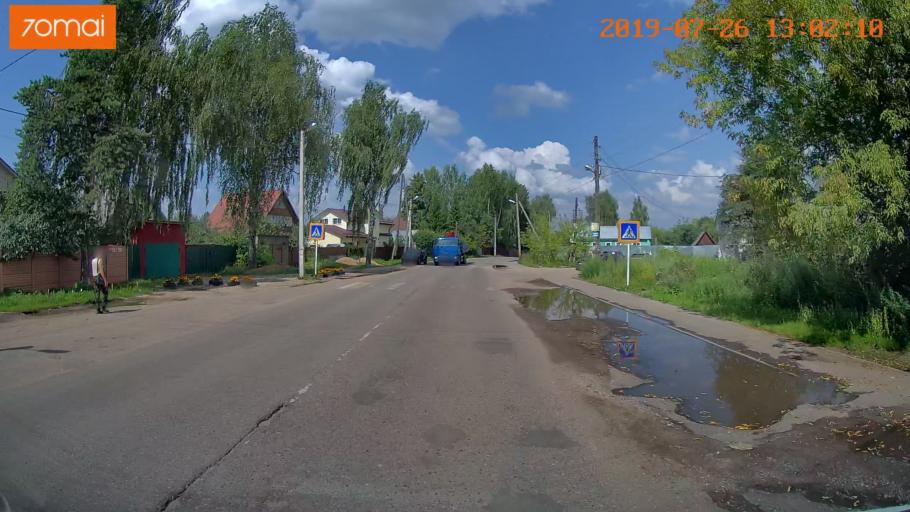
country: RU
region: Ivanovo
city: Bogorodskoye
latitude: 57.0432
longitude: 41.0116
